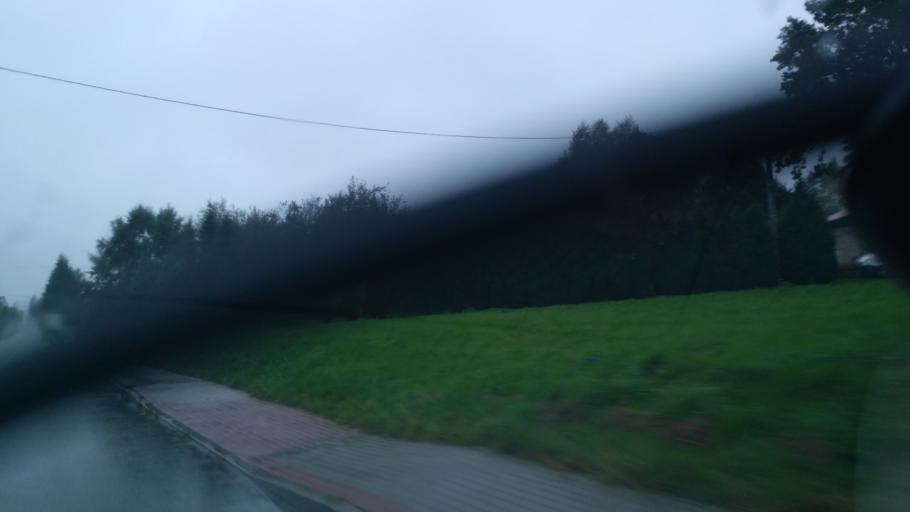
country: PL
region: Subcarpathian Voivodeship
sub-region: Powiat krosnienski
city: Kroscienko Wyzne
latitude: 49.6916
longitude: 21.8088
